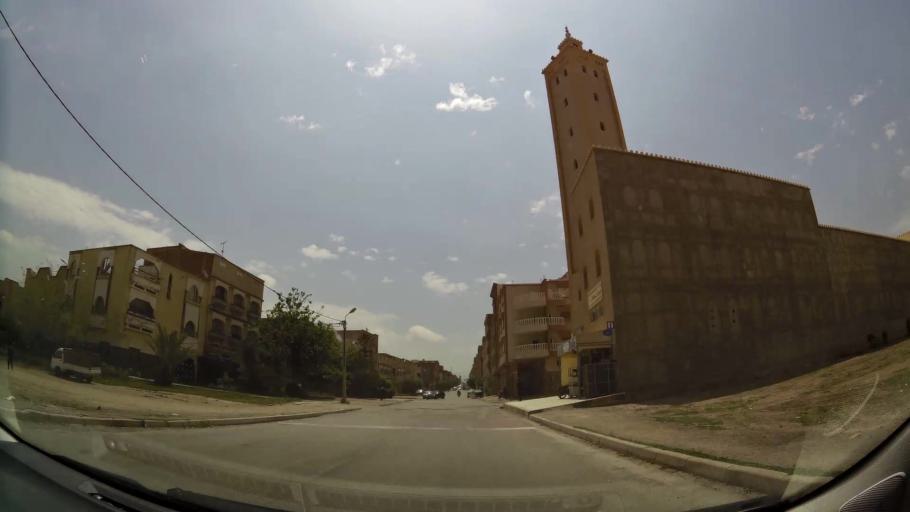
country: MA
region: Oriental
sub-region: Oujda-Angad
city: Oujda
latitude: 34.6897
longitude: -1.8862
